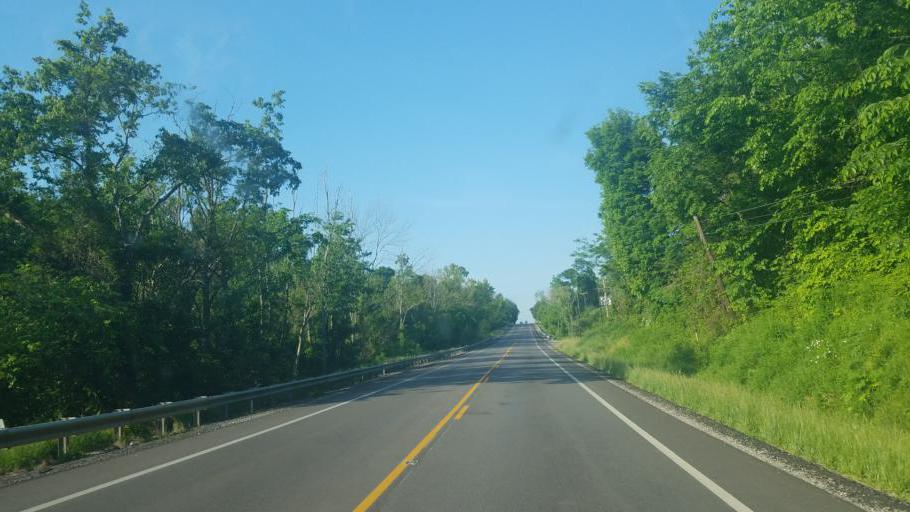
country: US
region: West Virginia
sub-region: Mason County
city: New Haven
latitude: 39.0838
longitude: -81.9262
